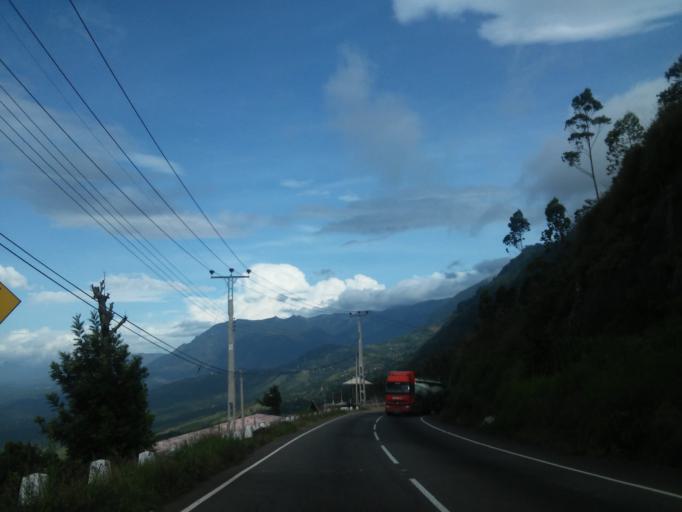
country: LK
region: Uva
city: Haputale
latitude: 6.7596
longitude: 80.9388
